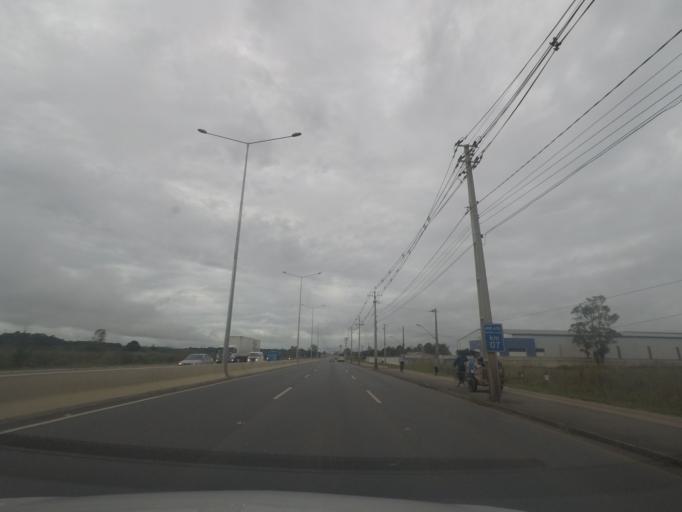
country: BR
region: Parana
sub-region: Pinhais
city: Pinhais
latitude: -25.4466
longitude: -49.1363
